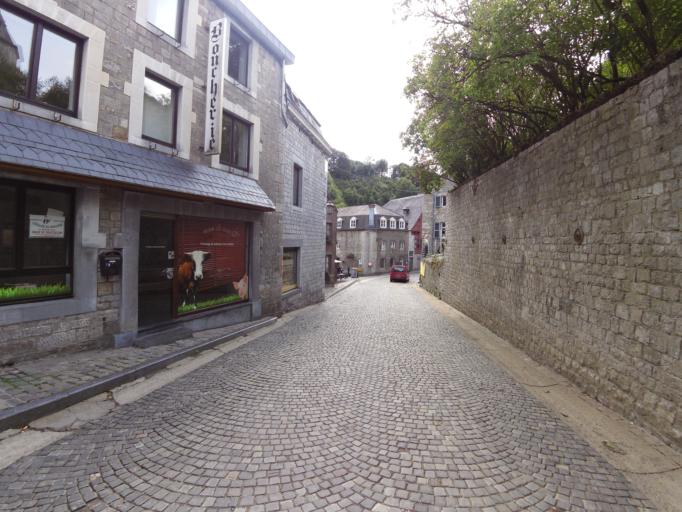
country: BE
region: Wallonia
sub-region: Province du Luxembourg
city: Durbuy
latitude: 50.3526
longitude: 5.4566
